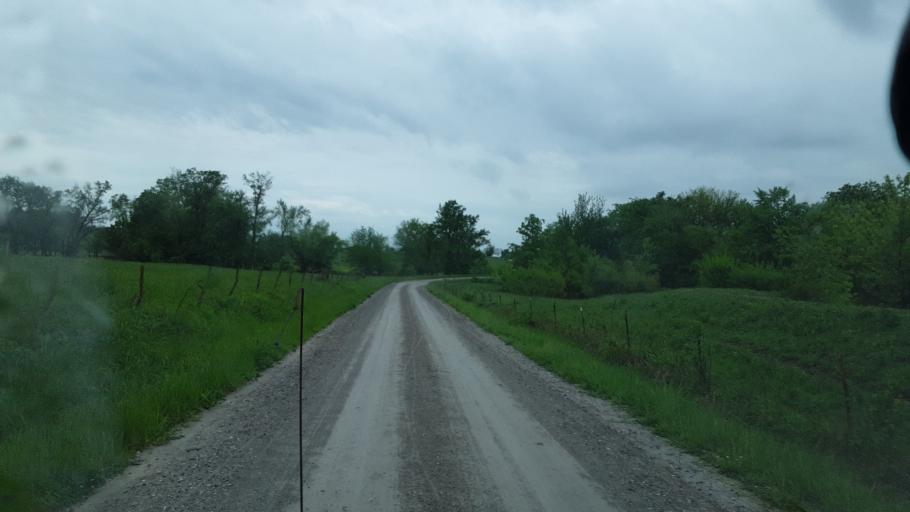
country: US
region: Missouri
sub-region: Randolph County
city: Moberly
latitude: 39.3167
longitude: -92.3037
